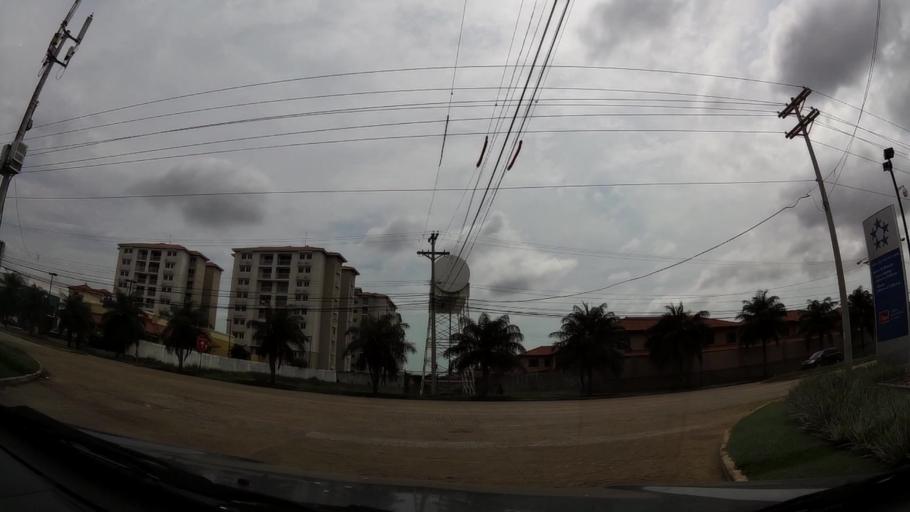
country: PA
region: Panama
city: San Miguelito
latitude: 9.0425
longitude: -79.4184
